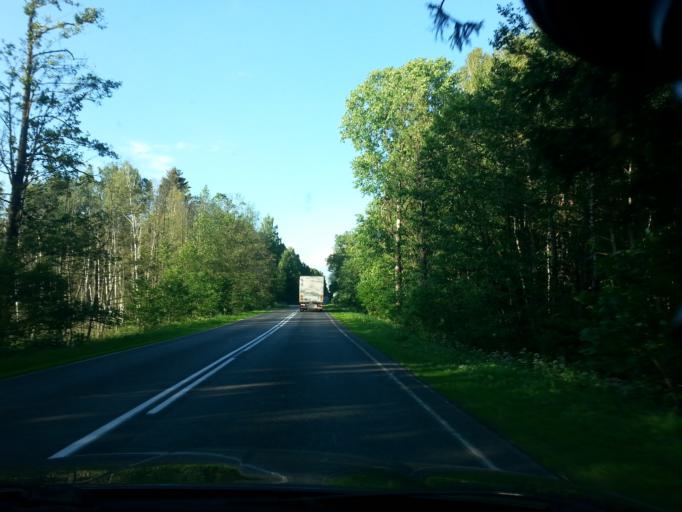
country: BY
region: Minsk
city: Svir
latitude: 54.8711
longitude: 26.3497
